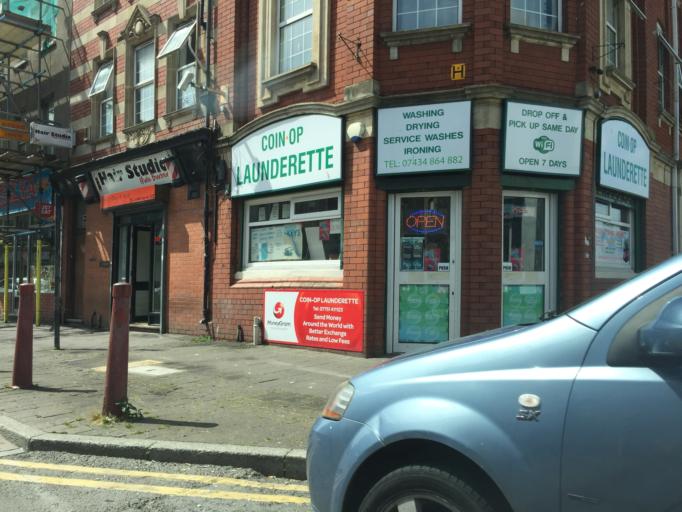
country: GB
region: Wales
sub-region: Newport
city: Newport
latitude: 51.5789
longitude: -2.9898
